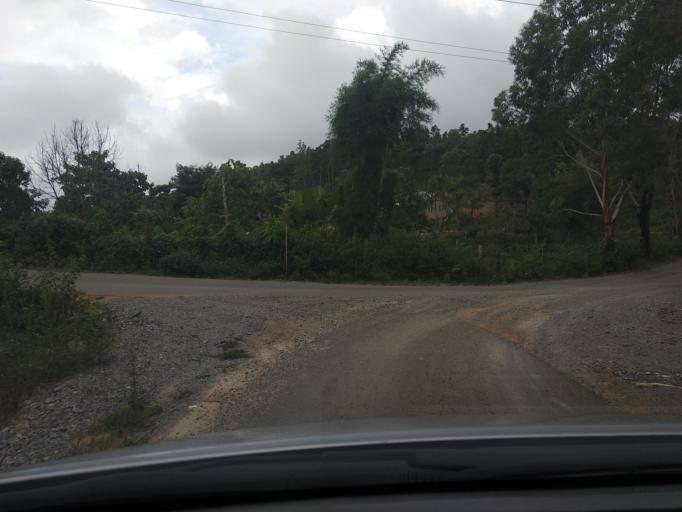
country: MM
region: Mandalay
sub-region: Pyin Oo Lwin District
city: Pyin Oo Lwin
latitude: 21.9141
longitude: 96.3832
